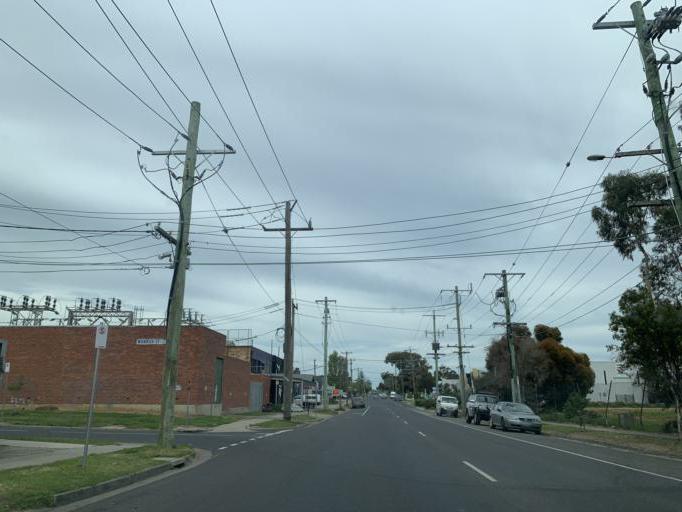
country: AU
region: Victoria
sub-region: Bayside
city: Highett
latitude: -37.9566
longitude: 145.0388
